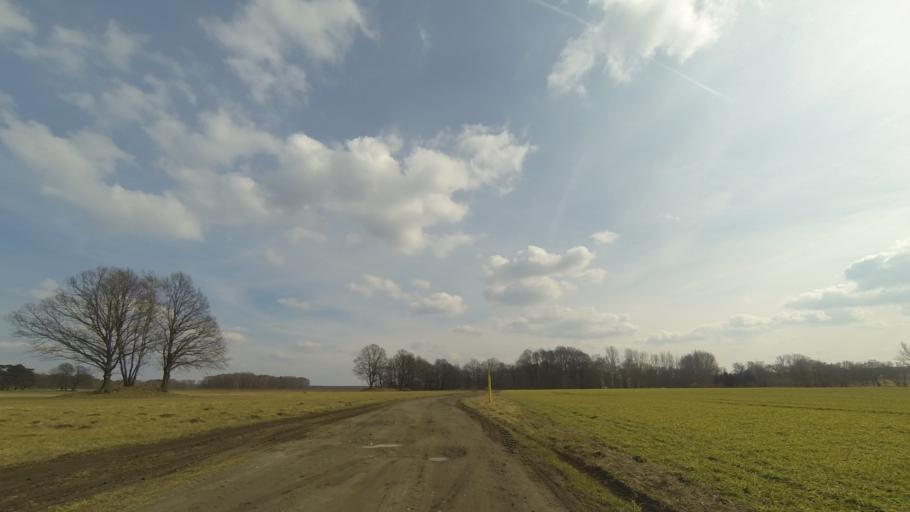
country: DE
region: Saxony
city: Radeburg
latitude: 51.2276
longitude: 13.7104
